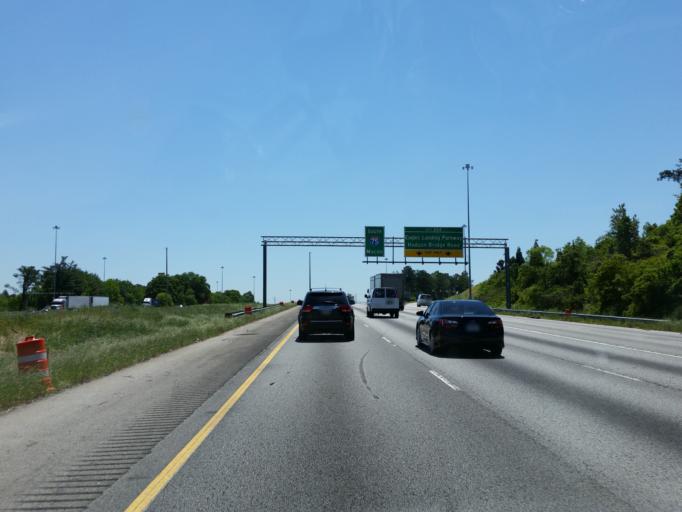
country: US
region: Georgia
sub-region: Henry County
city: Stockbridge
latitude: 33.5098
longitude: -84.2358
